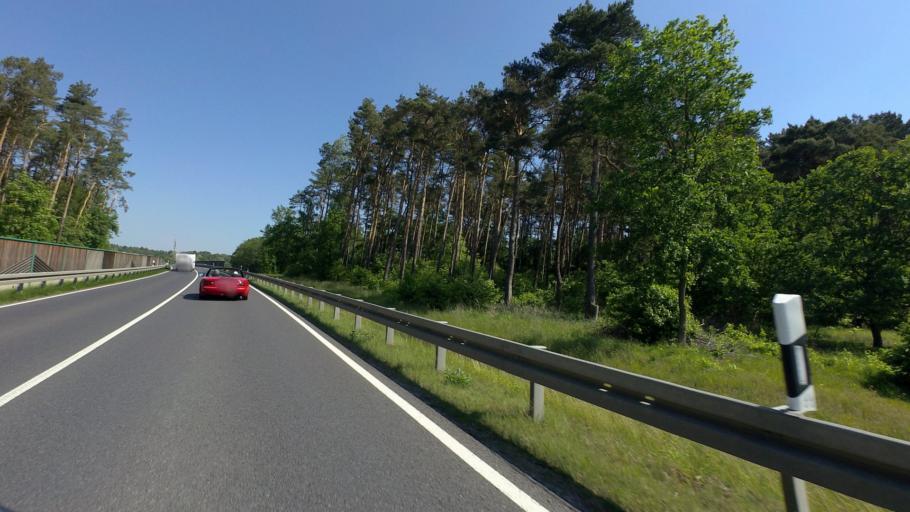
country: DE
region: Saxony
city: Bernsdorf
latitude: 51.3756
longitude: 14.0818
